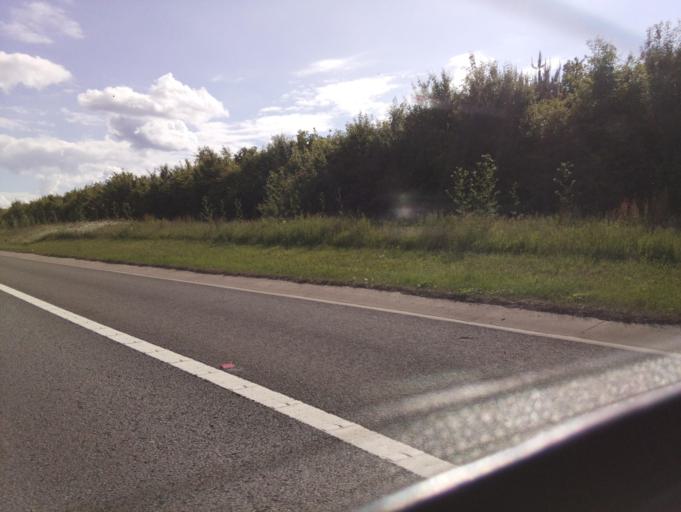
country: GB
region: England
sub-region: Hertfordshire
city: Redbourn
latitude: 51.7774
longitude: -0.4109
